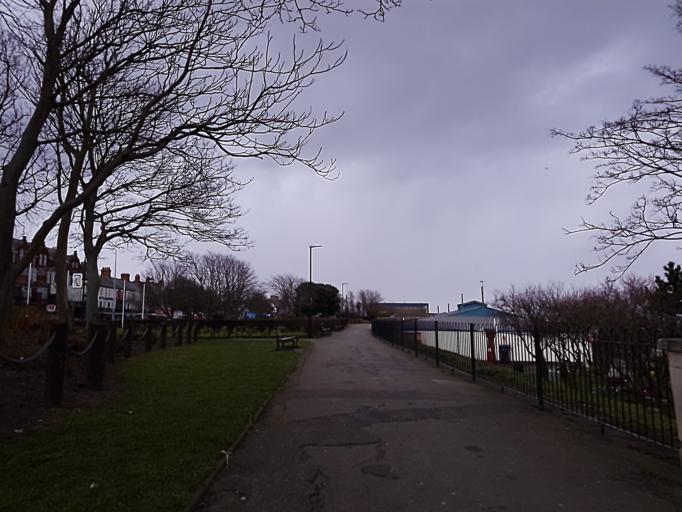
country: GB
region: England
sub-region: North East Lincolnshire
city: Cleethorpes
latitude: 53.5593
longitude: -0.0265
